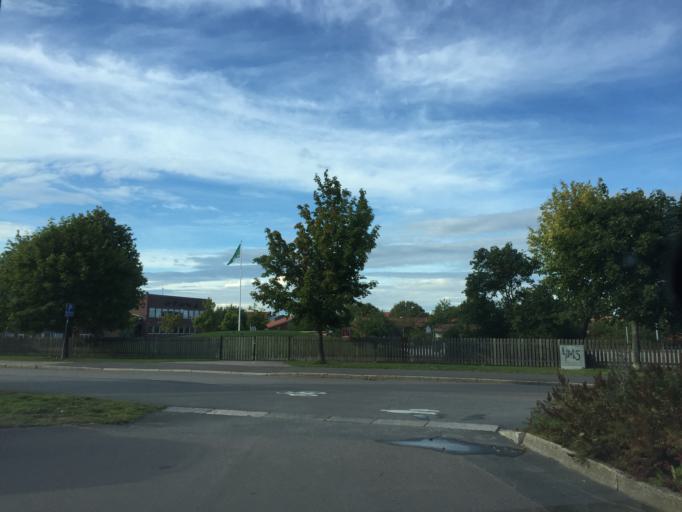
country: SE
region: Soedermanland
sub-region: Eskilstuna Kommun
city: Eskilstuna
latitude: 59.3738
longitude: 16.4818
